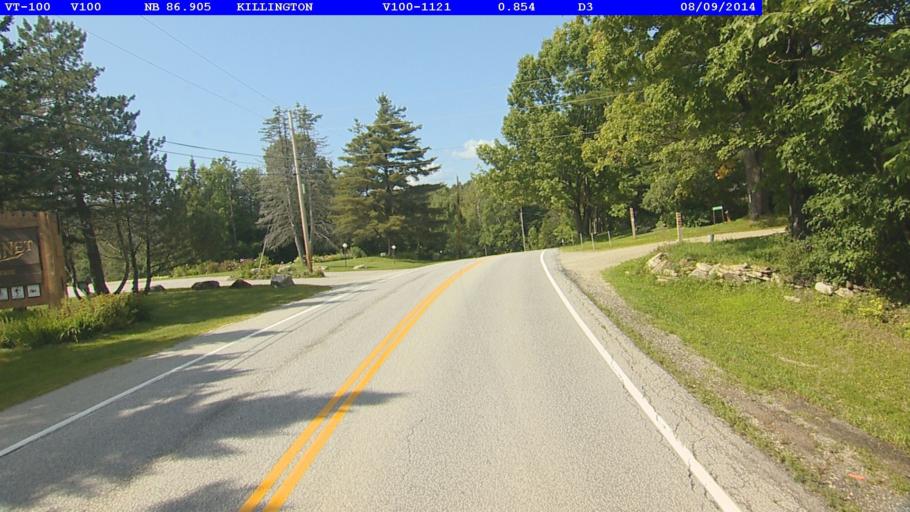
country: US
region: Vermont
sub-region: Rutland County
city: Rutland
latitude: 43.6789
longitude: -72.8107
